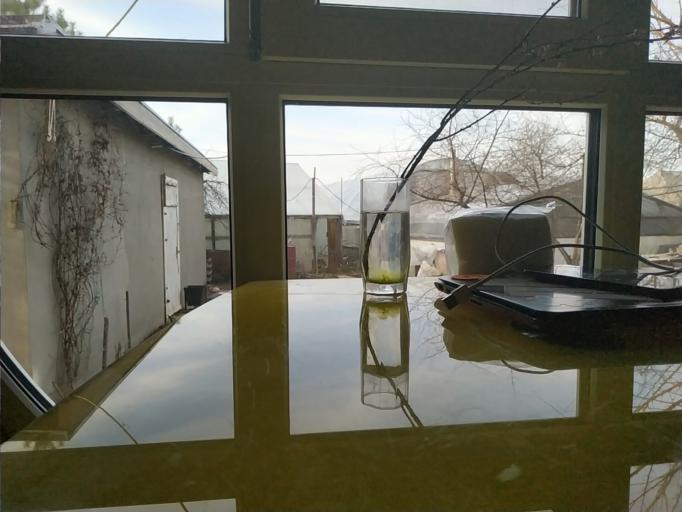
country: RU
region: Republic of Karelia
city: Suoyarvi
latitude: 61.7672
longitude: 32.3160
